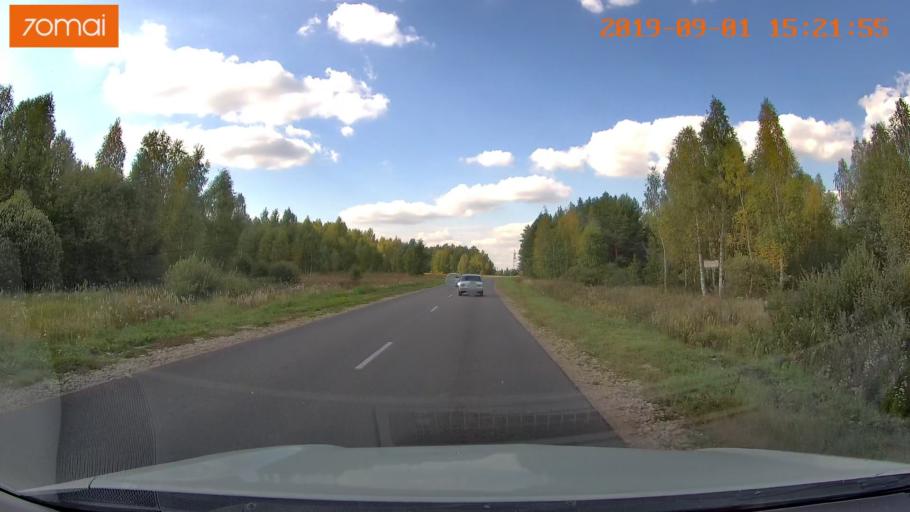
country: RU
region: Kaluga
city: Maloyaroslavets
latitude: 54.9323
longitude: 36.4693
